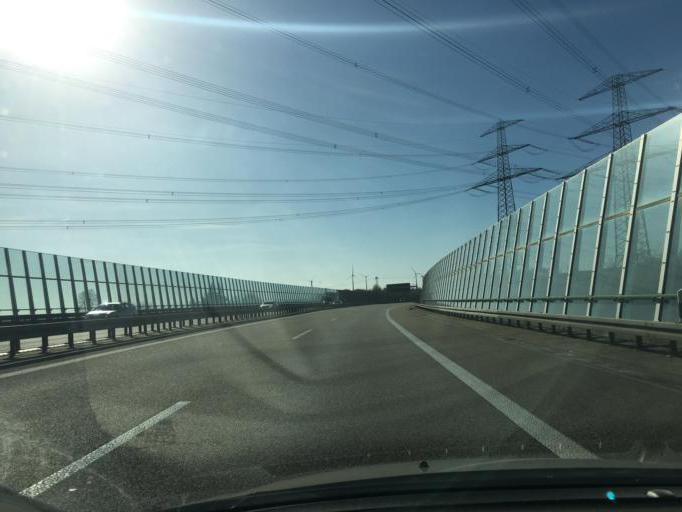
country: DE
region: Saxony
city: Hartmannsdorf
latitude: 50.8643
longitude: 12.8146
